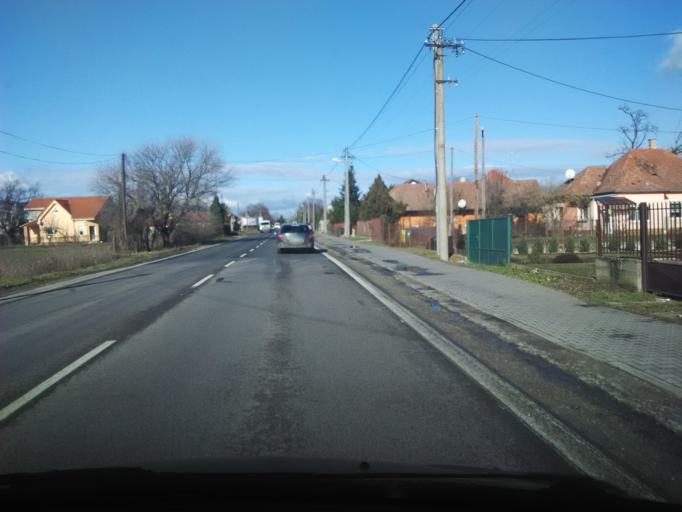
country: SK
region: Nitriansky
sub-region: Okres Nitra
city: Nitra
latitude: 48.2325
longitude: 18.1286
